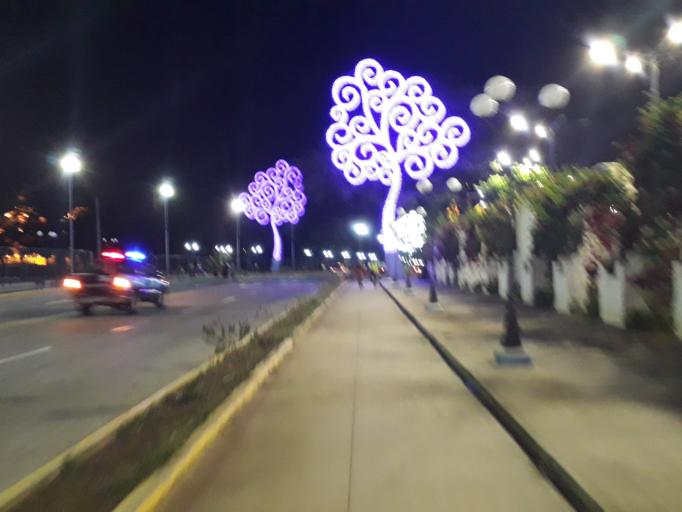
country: NI
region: Managua
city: Managua
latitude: 12.1569
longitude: -86.2678
